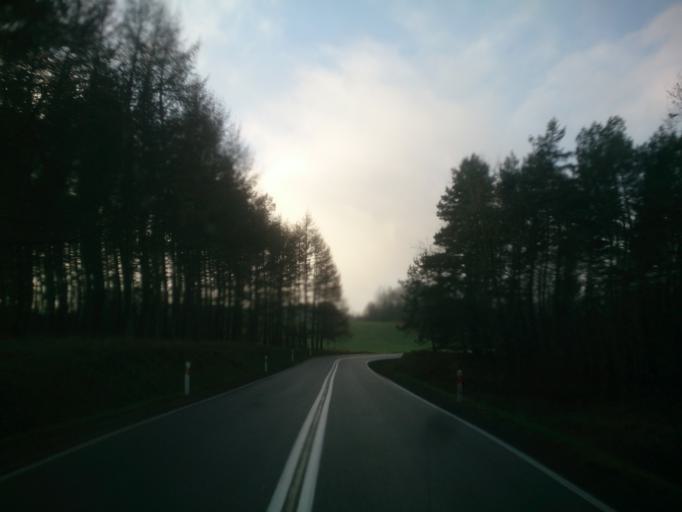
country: PL
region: Pomeranian Voivodeship
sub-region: Powiat bytowski
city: Tuchomie
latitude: 54.0686
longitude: 17.2765
